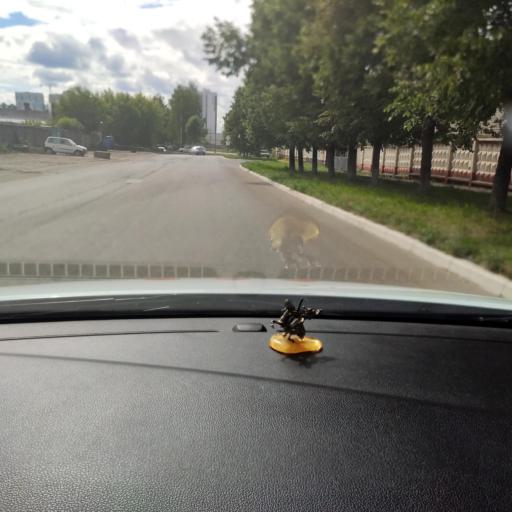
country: RU
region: Tatarstan
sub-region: Gorod Kazan'
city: Kazan
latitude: 55.7730
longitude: 49.1905
